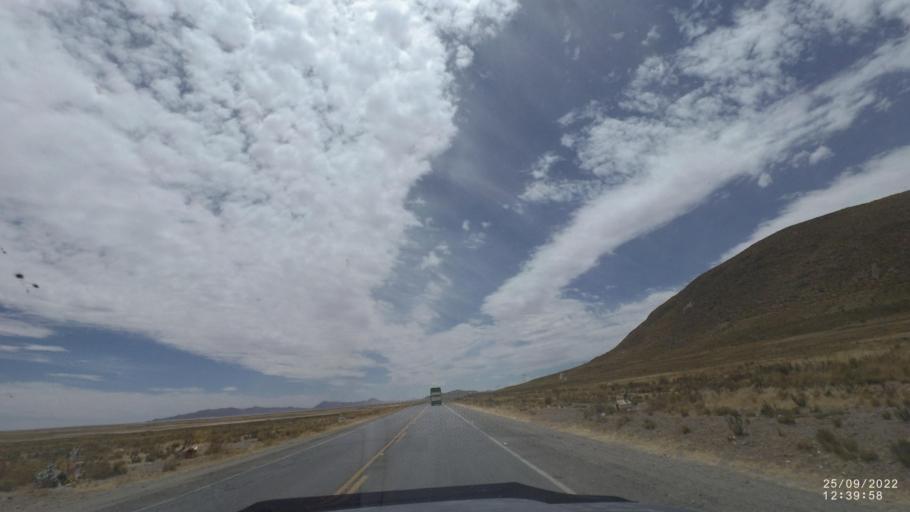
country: BO
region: Oruro
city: Machacamarca
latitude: -18.1226
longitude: -67.0066
